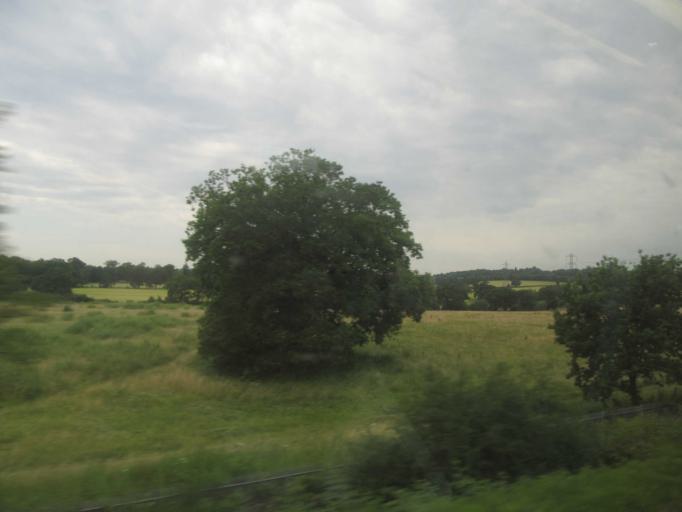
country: GB
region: England
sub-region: Greater London
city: Edgware
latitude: 51.6316
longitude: -0.2668
